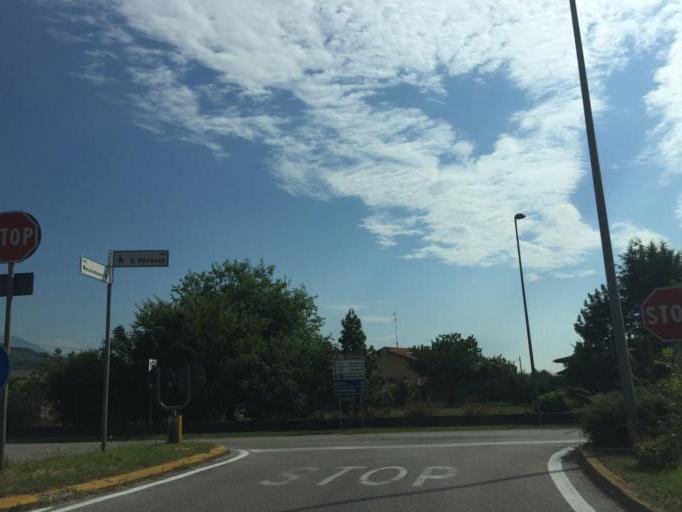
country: IT
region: Friuli Venezia Giulia
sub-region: Provincia di Pordenone
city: Caneva
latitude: 45.9619
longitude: 12.4487
